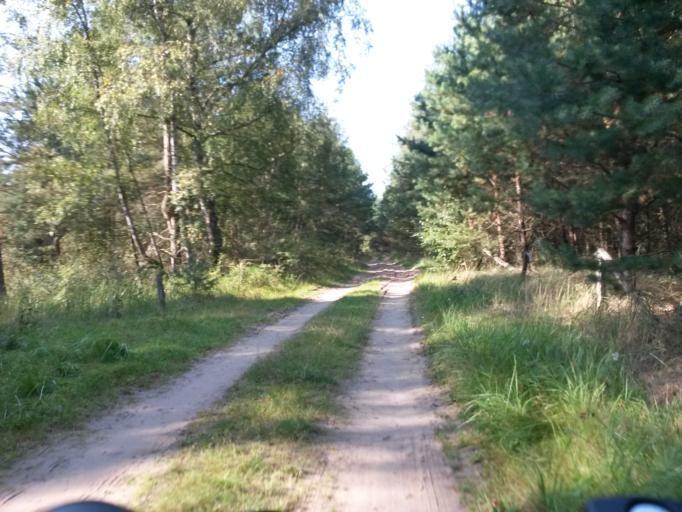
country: DE
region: Brandenburg
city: Templin
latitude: 53.0845
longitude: 13.4070
